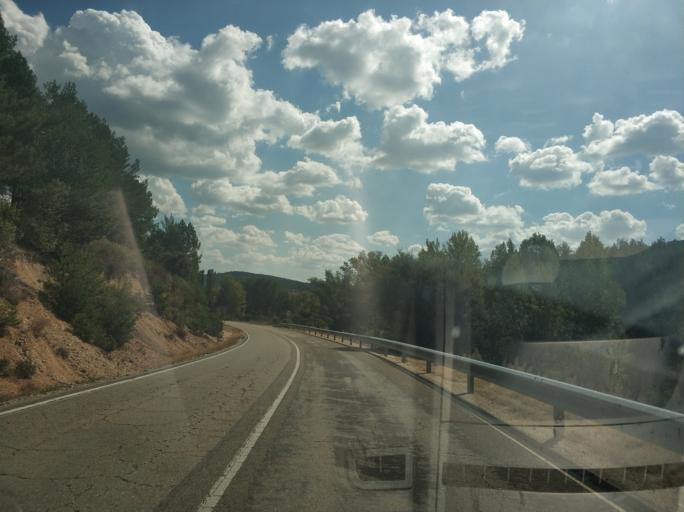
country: ES
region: Castille and Leon
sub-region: Provincia de Soria
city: Casarejos
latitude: 41.7995
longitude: -3.0396
